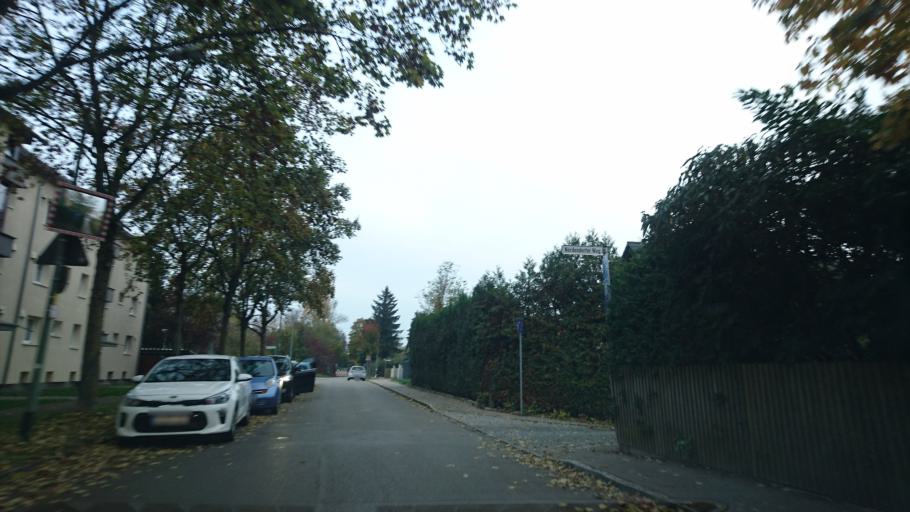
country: DE
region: Bavaria
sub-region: Swabia
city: Gersthofen
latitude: 48.4023
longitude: 10.8845
